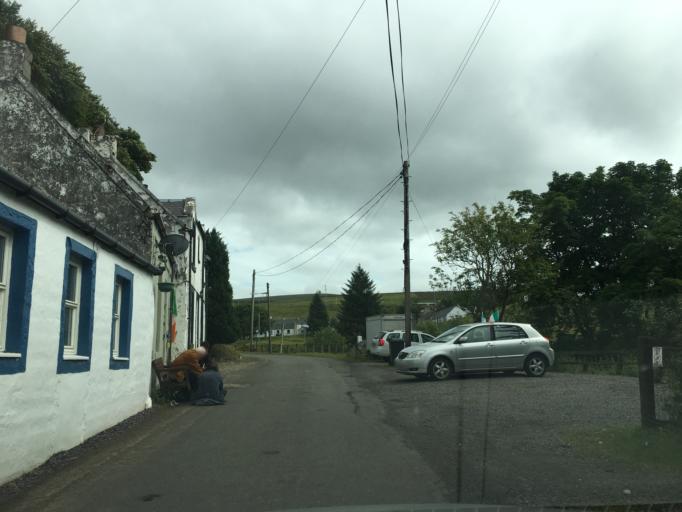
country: GB
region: Scotland
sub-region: Dumfries and Galloway
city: Sanquhar
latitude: 55.3981
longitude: -3.7827
